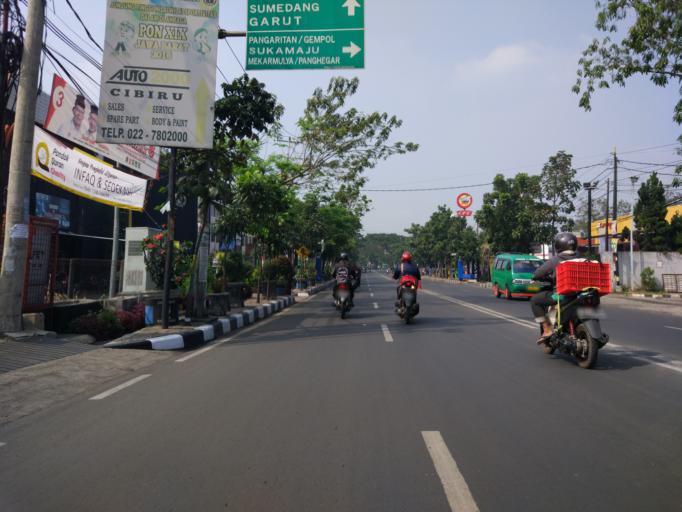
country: ID
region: West Java
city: Cileunyi
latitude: -6.9260
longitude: 107.7108
